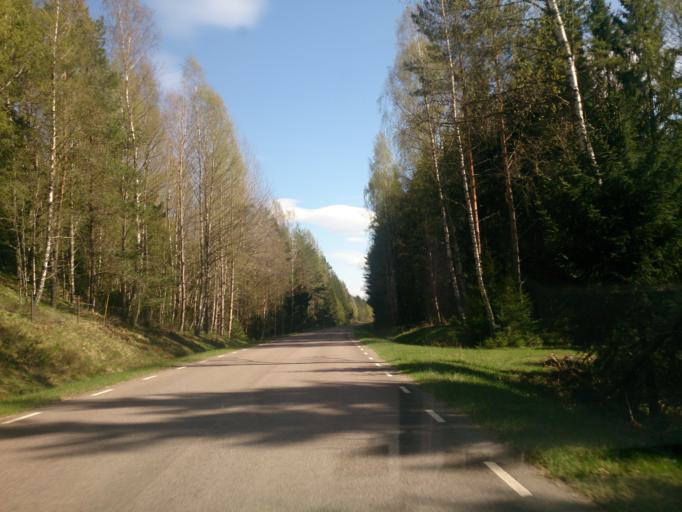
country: SE
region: OEstergoetland
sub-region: Linkopings Kommun
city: Ljungsbro
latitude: 58.5988
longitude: 15.4930
